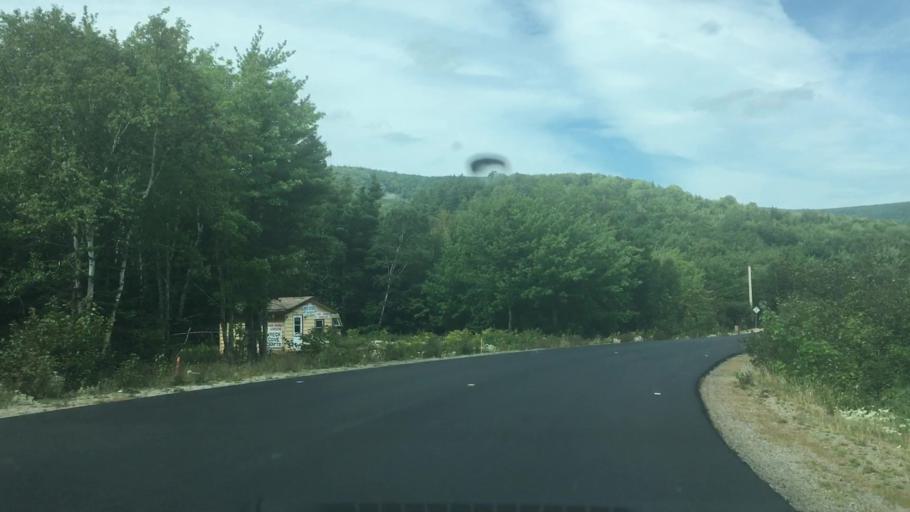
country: CA
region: Nova Scotia
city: Sydney Mines
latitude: 46.5441
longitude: -60.4156
